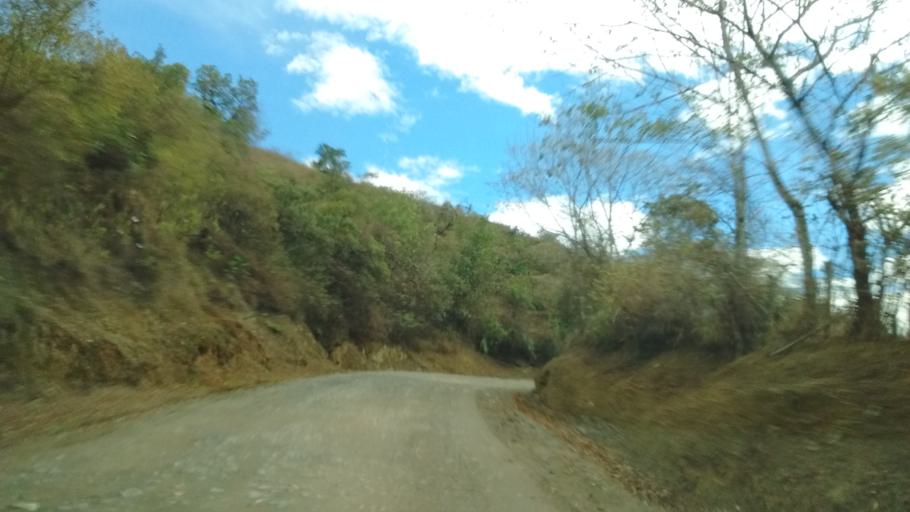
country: CO
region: Cauca
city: Almaguer
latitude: 1.8594
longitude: -76.9302
